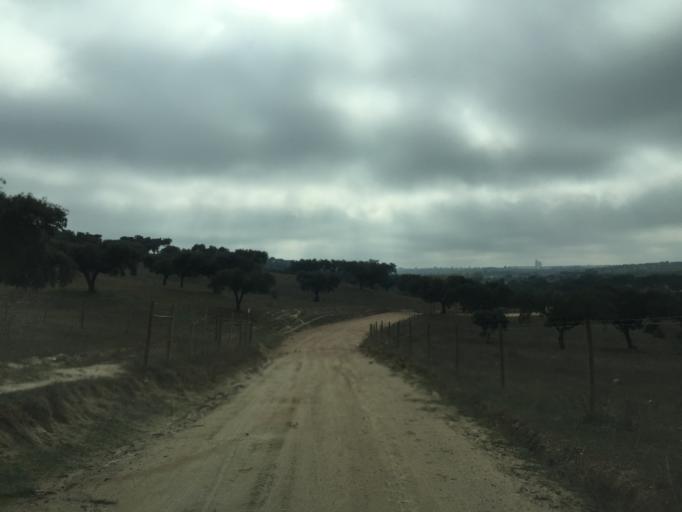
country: PT
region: Portalegre
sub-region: Fronteira
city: Fronteira
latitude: 39.0686
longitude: -7.6236
